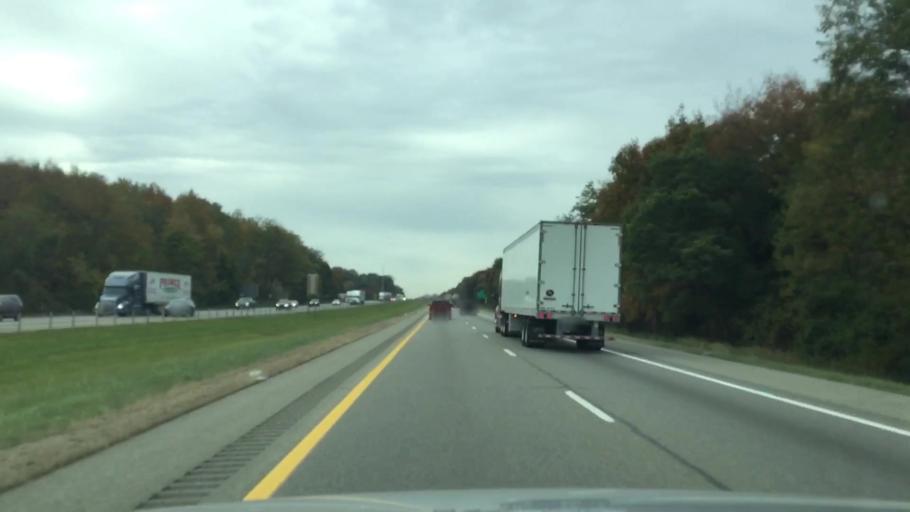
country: US
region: Michigan
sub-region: Calhoun County
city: Lakeview
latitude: 42.2635
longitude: -85.2106
